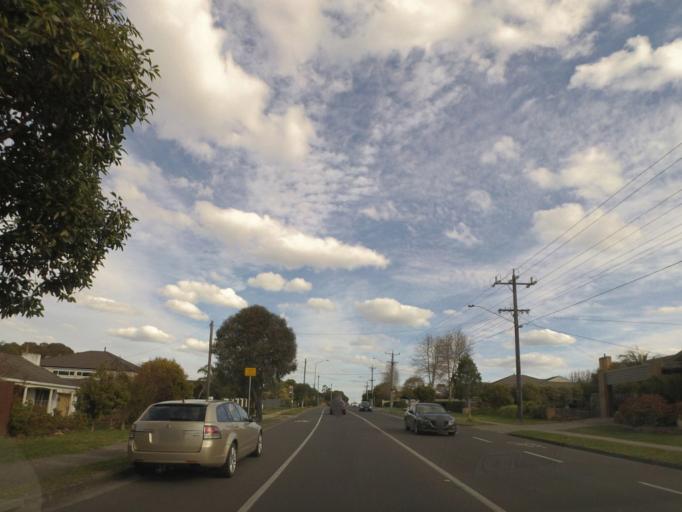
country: AU
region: Victoria
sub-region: Manningham
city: Doncaster East
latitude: -37.7826
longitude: 145.1445
